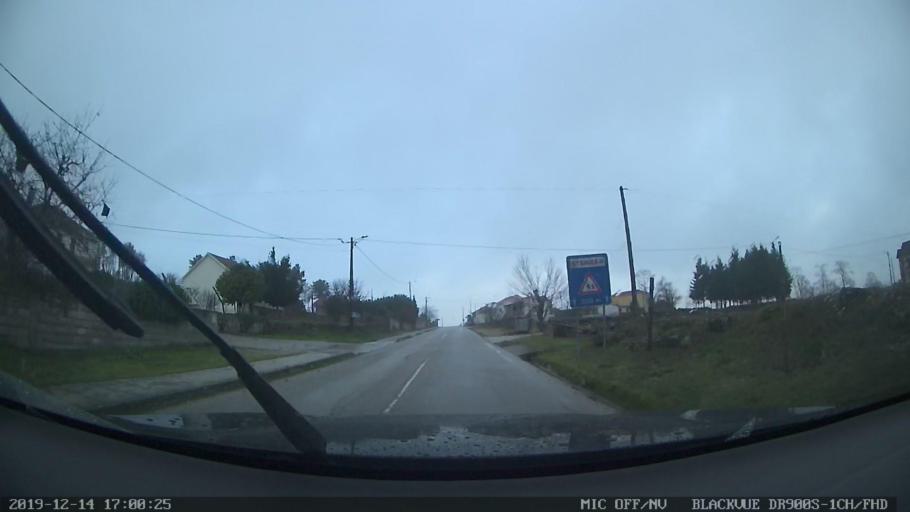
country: PT
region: Vila Real
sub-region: Vila Pouca de Aguiar
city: Vila Pouca de Aguiar
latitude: 41.4404
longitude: -7.5717
